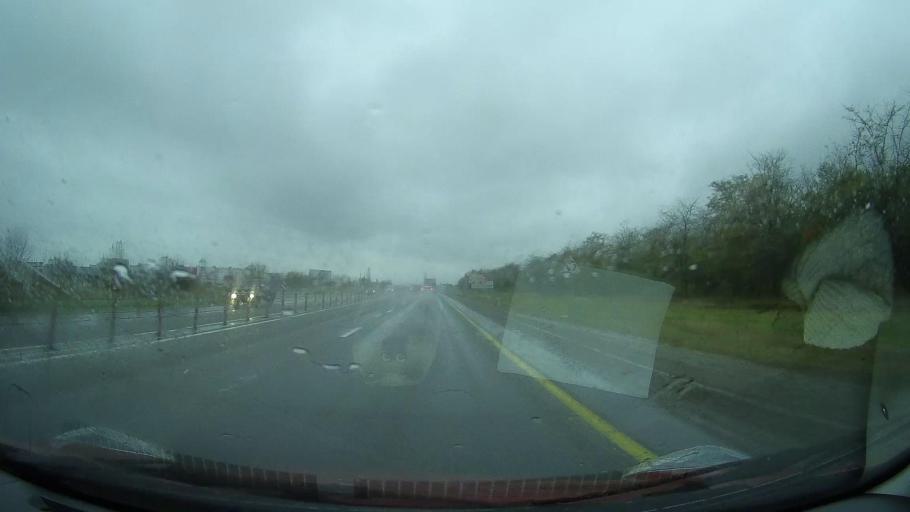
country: RU
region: Stavropol'skiy
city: Nevinnomyssk
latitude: 44.6411
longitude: 41.9659
